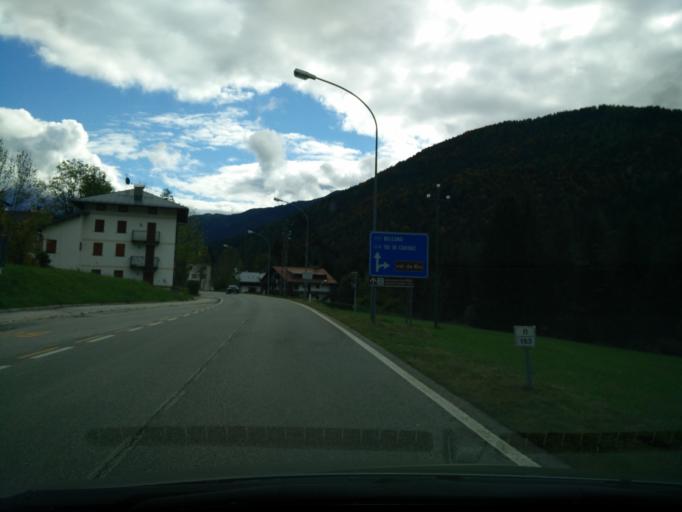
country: IT
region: Veneto
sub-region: Provincia di Belluno
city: Auronzo
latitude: 46.5694
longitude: 12.4004
